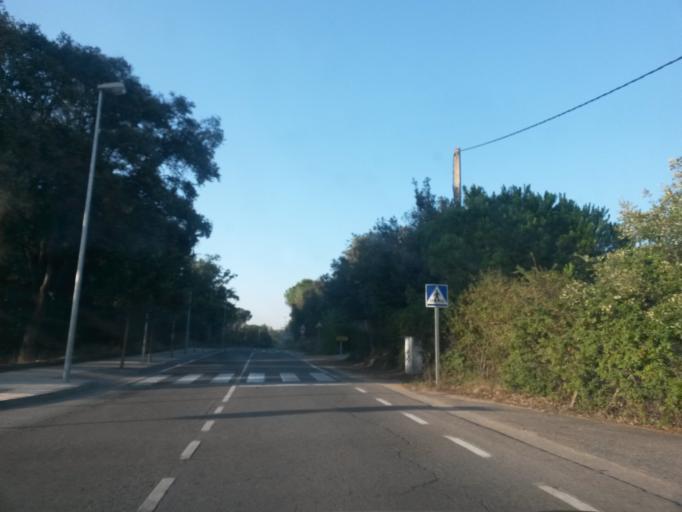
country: ES
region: Catalonia
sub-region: Provincia de Girona
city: Fornells de la Selva
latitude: 41.9450
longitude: 2.8128
